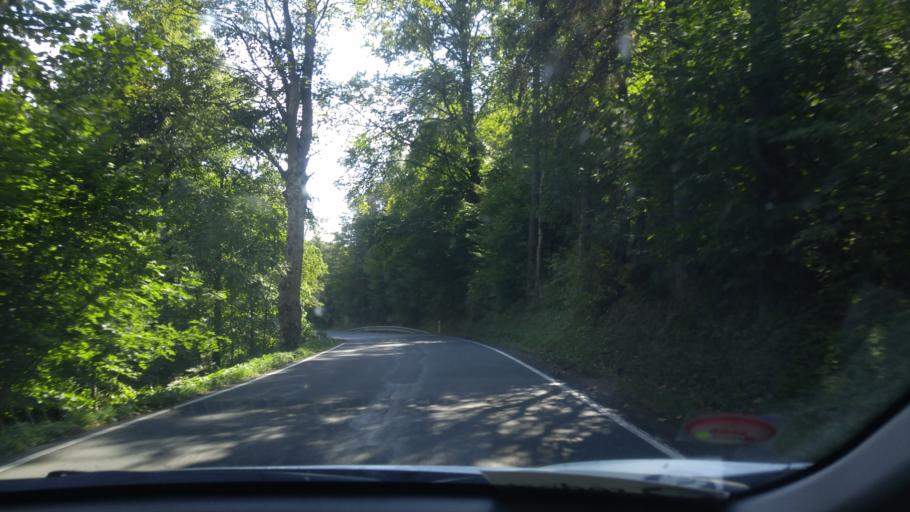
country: CZ
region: Olomoucky
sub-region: Okres Sumperk
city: Stare Mesto
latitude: 50.1662
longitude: 17.0269
